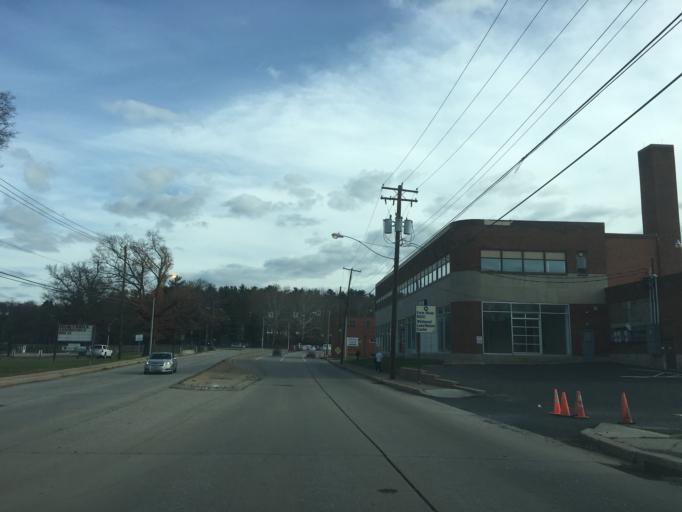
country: US
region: Pennsylvania
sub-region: Dauphin County
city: Harrisburg
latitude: 40.2824
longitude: -76.8833
